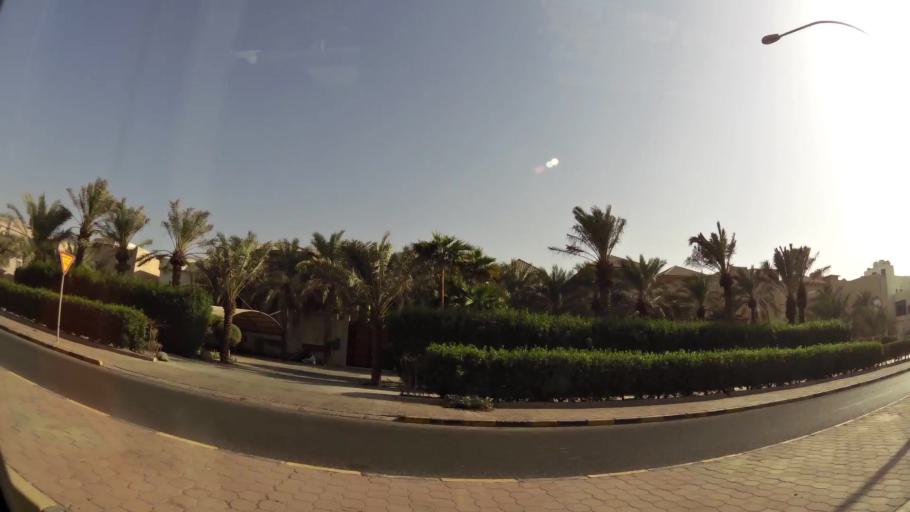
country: KW
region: Muhafazat Hawalli
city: Ar Rumaythiyah
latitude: 29.3087
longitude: 48.0698
